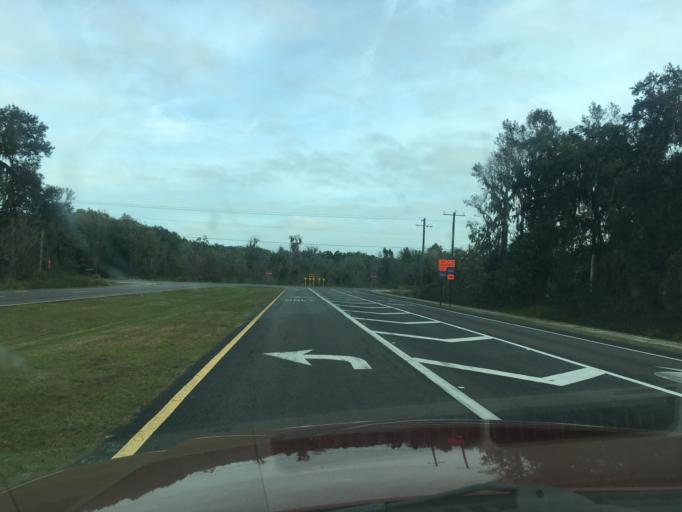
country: US
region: Florida
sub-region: Hillsborough County
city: Plant City
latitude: 28.0465
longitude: -82.1041
